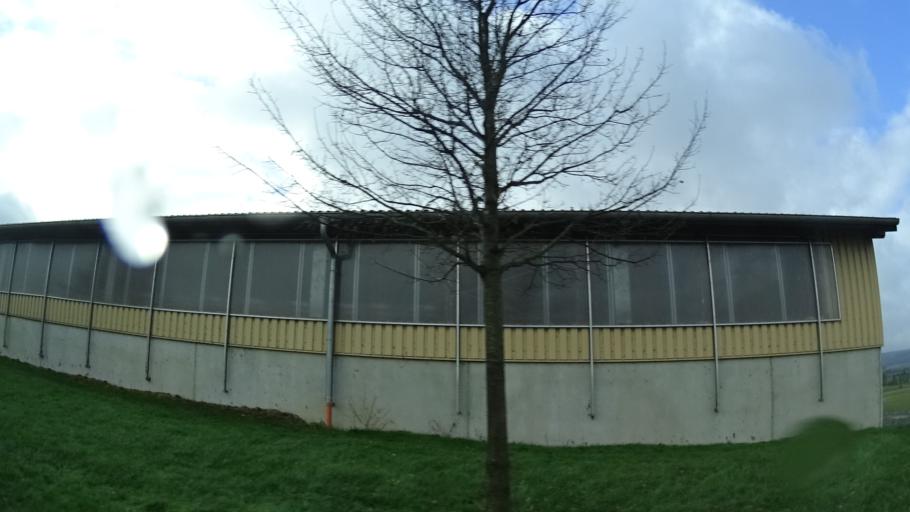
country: DE
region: Hesse
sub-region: Regierungsbezirk Kassel
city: Neuhof
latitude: 50.4339
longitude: 9.6138
